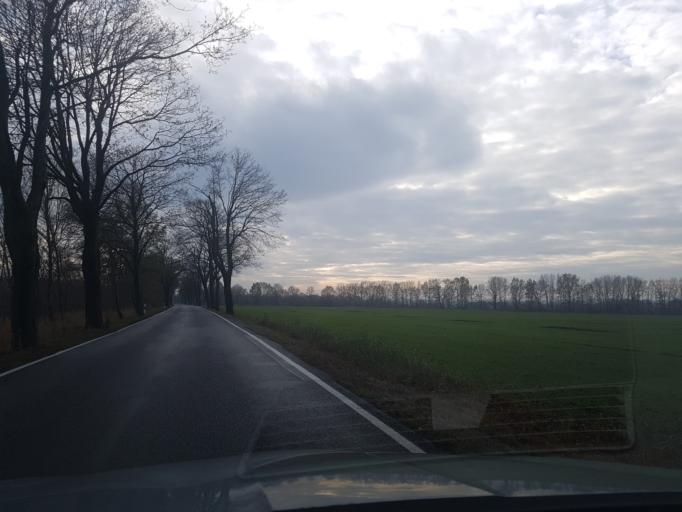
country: DE
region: Brandenburg
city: Plessa
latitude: 51.4390
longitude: 13.6232
